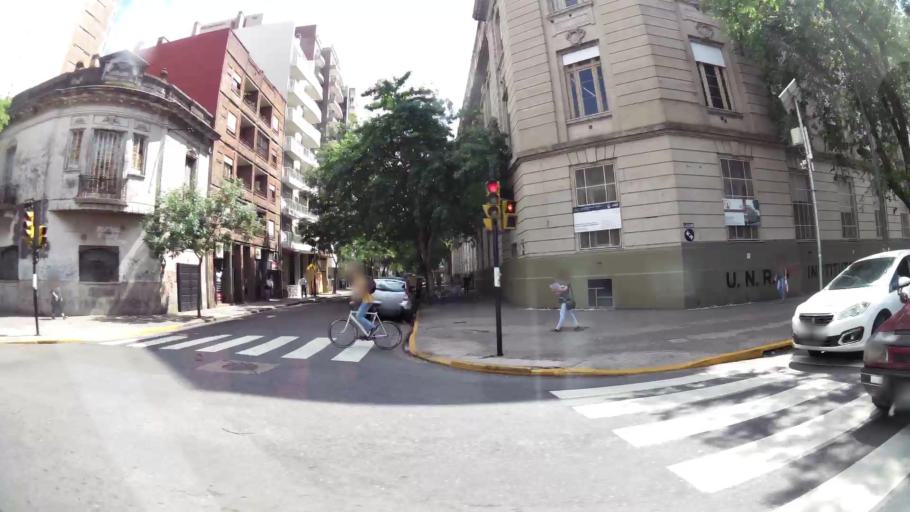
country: AR
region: Santa Fe
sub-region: Departamento de Rosario
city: Rosario
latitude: -32.9593
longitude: -60.6296
